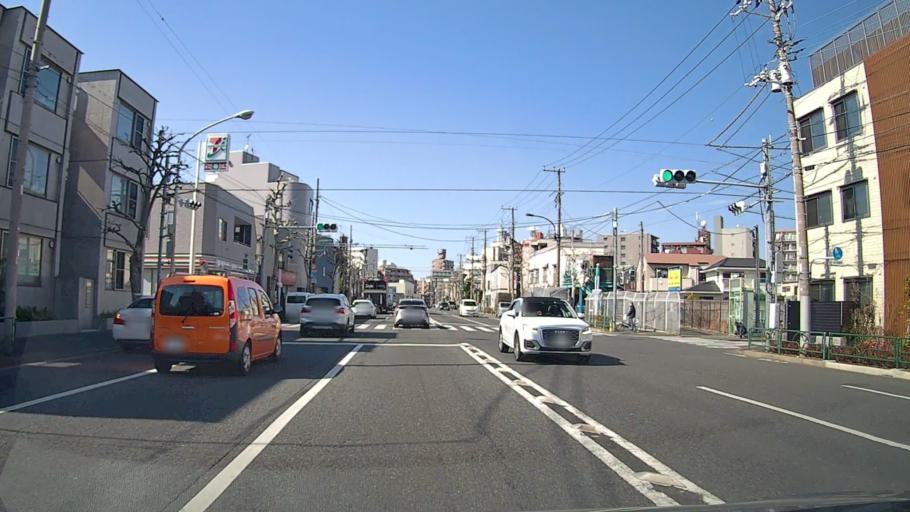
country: JP
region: Tokyo
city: Tokyo
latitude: 35.7210
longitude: 139.6864
